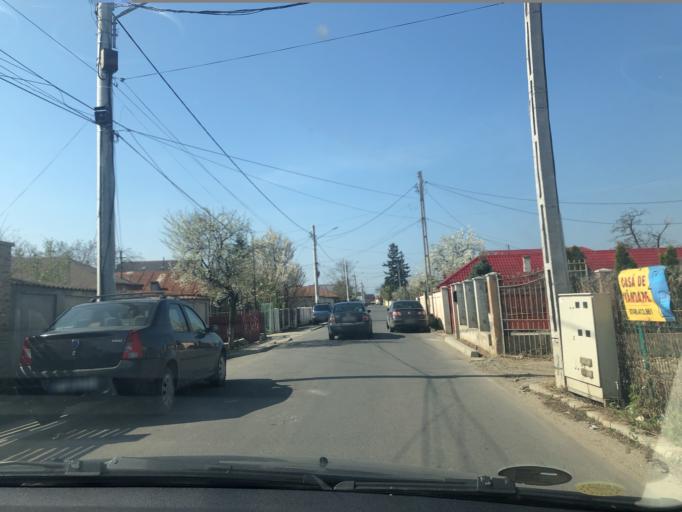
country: RO
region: Ilfov
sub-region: Comuna Clinceni
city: Clinceni
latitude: 44.3742
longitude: 25.9608
